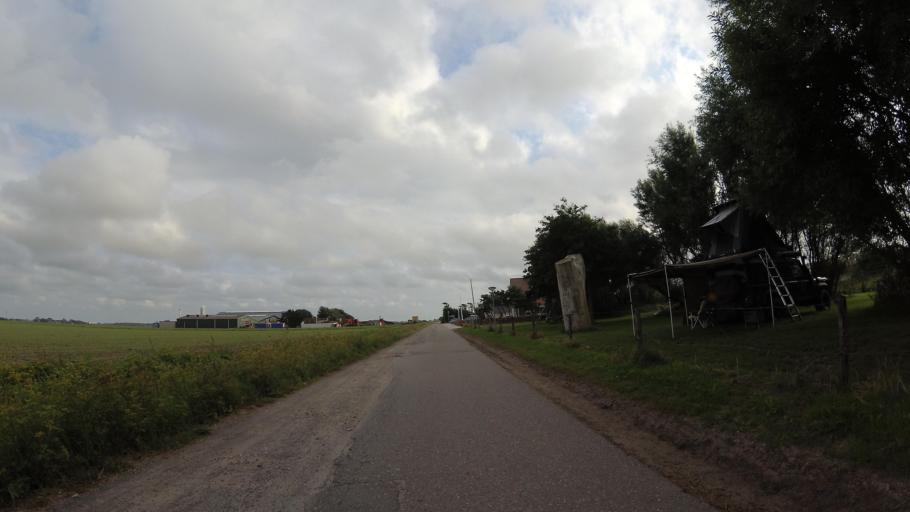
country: NL
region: North Holland
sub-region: Gemeente Den Helder
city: Den Helder
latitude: 52.8781
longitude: 4.7266
